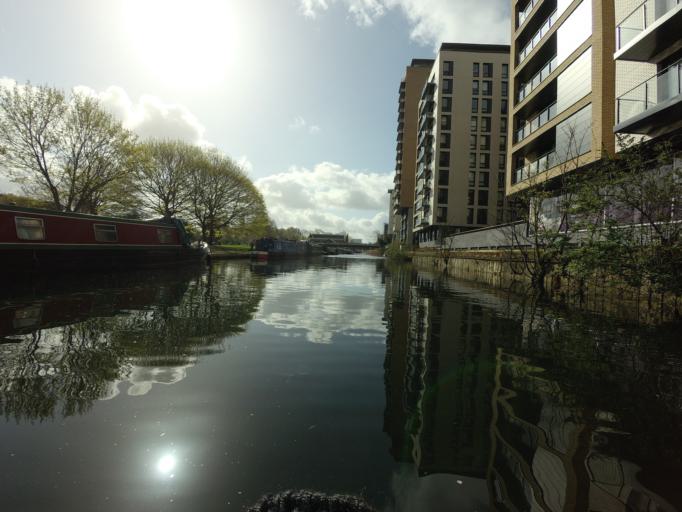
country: GB
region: England
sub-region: Greater London
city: Bethnal Green
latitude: 51.5290
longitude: -0.0413
